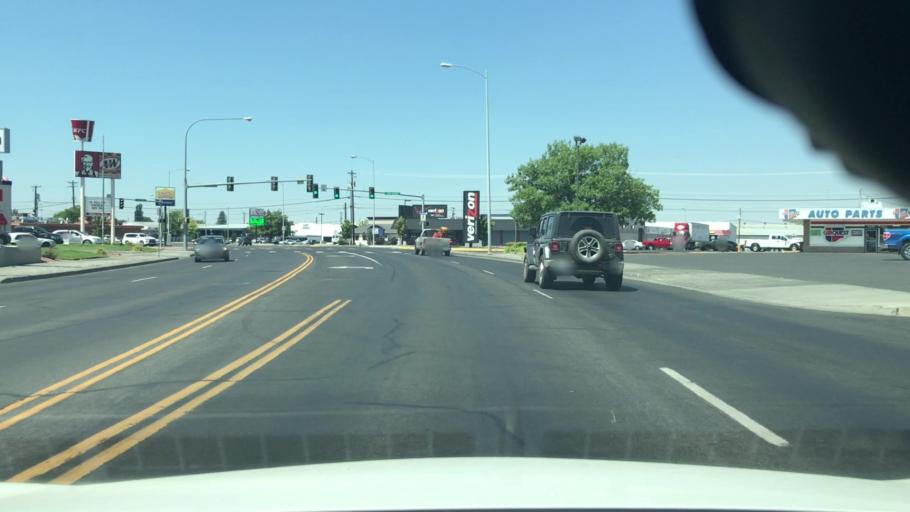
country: US
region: Washington
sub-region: Grant County
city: Moses Lake
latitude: 47.1323
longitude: -119.2724
